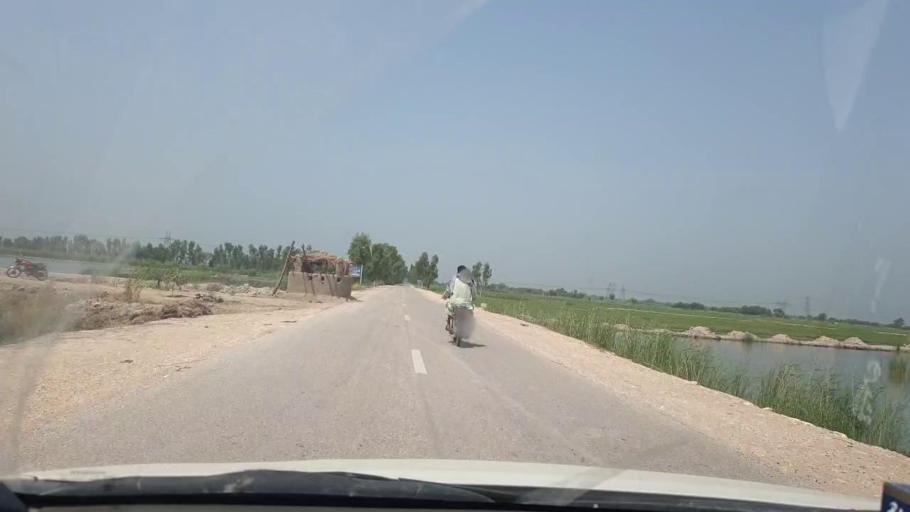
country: PK
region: Sindh
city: Rustam jo Goth
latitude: 27.9582
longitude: 68.7486
